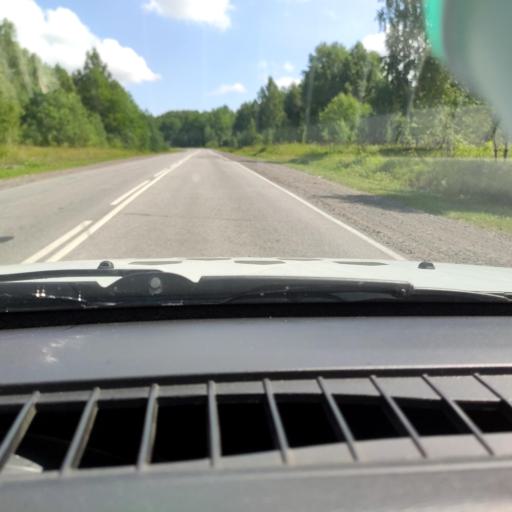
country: RU
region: Bashkortostan
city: Verkhniye Kigi
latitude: 55.3870
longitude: 58.6654
